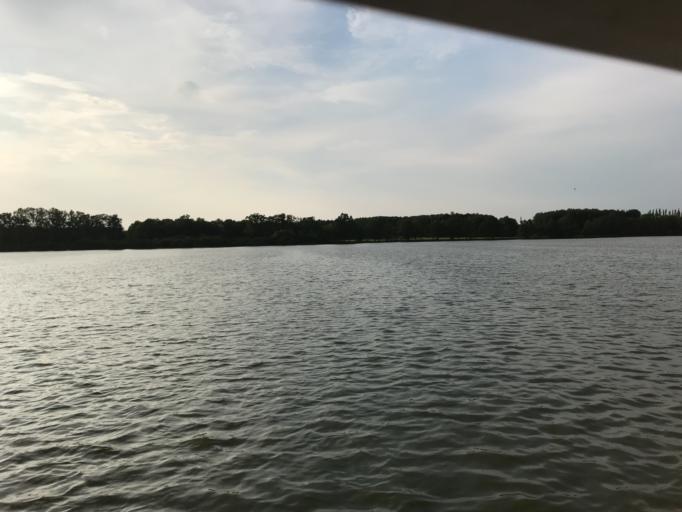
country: CZ
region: Jihocesky
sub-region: Okres Jindrichuv Hradec
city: Trebon
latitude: 48.9945
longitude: 14.7559
